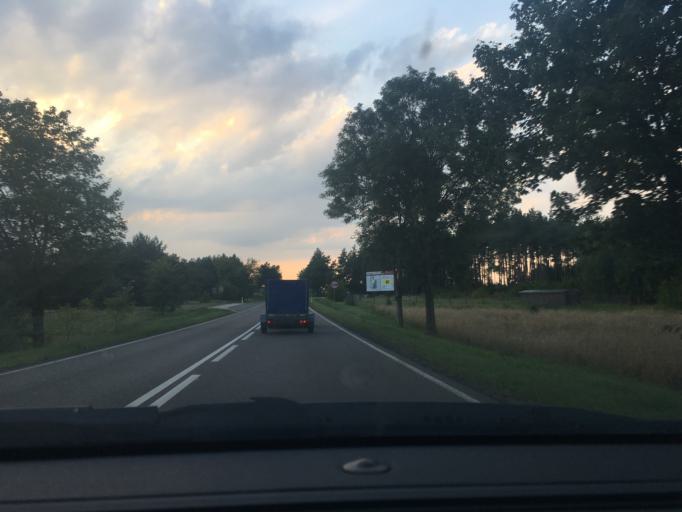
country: PL
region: Podlasie
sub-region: Powiat grajewski
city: Grajewo
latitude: 53.6196
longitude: 22.4960
